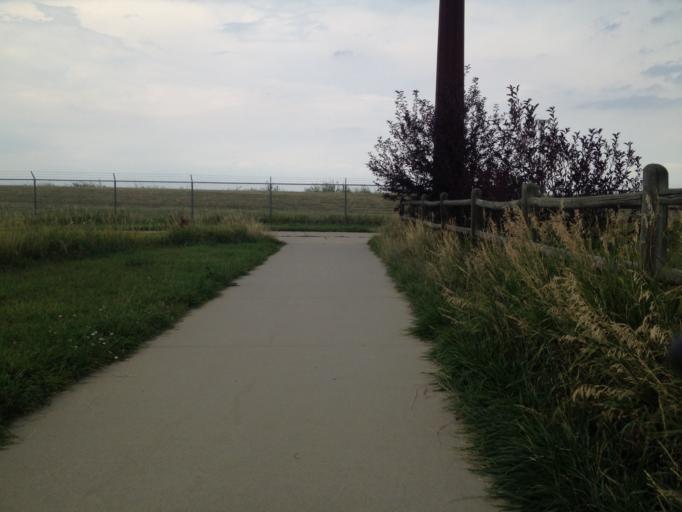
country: US
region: Colorado
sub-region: Boulder County
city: Louisville
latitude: 39.9896
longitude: -105.1563
